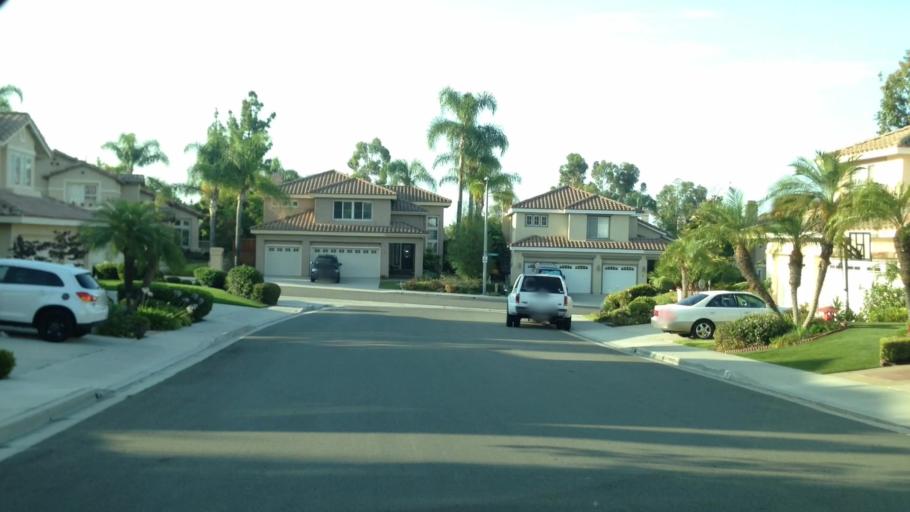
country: US
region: California
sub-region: Orange County
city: Rancho Santa Margarita
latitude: 33.6437
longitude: -117.6187
